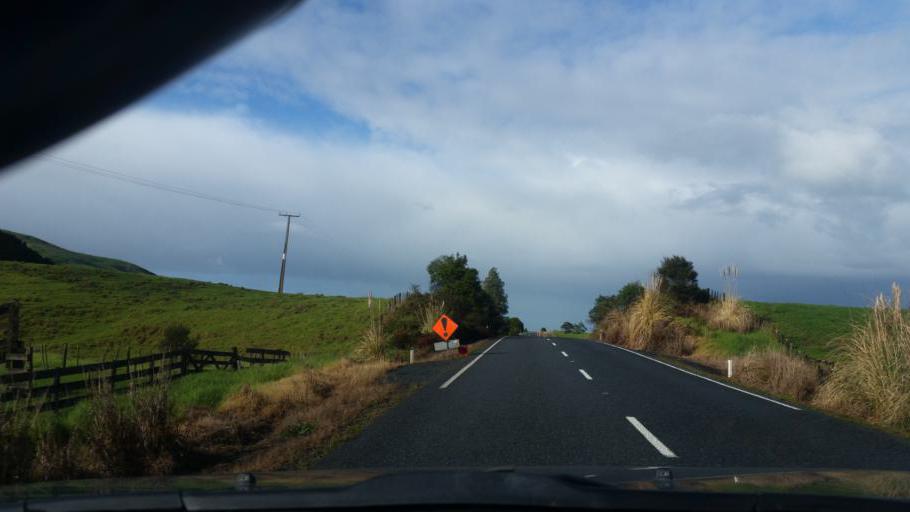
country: NZ
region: Northland
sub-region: Kaipara District
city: Dargaville
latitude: -35.8105
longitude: 173.9236
